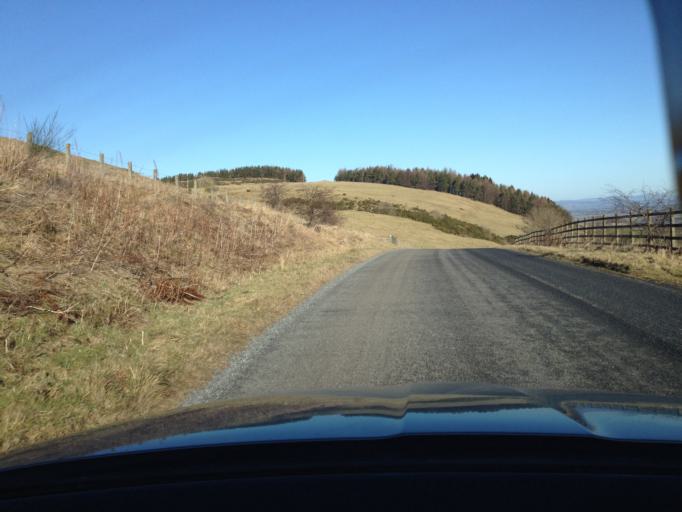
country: GB
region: Scotland
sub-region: Perth and Kinross
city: Bridge of Earn
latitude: 56.3073
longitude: -3.3860
